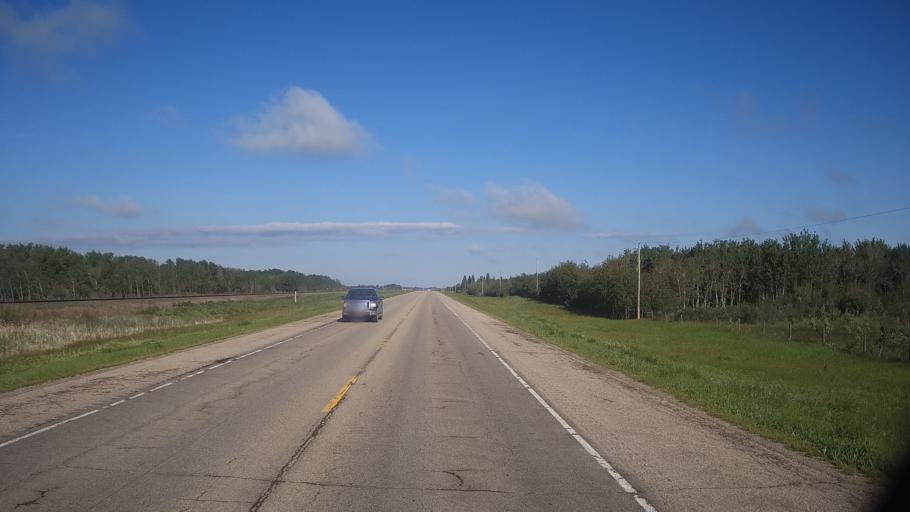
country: CA
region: Saskatchewan
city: Lanigan
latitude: 51.8557
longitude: -105.0894
